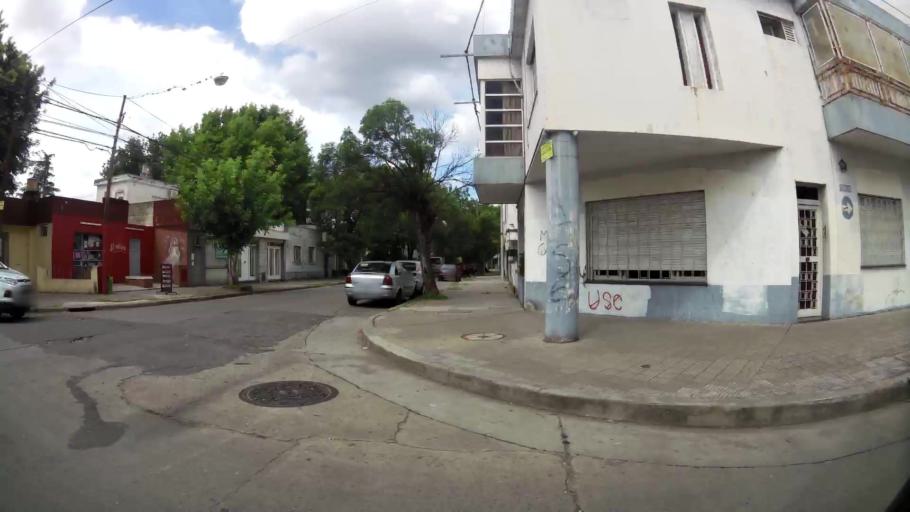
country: AR
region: Santa Fe
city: Gobernador Galvez
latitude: -32.9984
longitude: -60.6319
